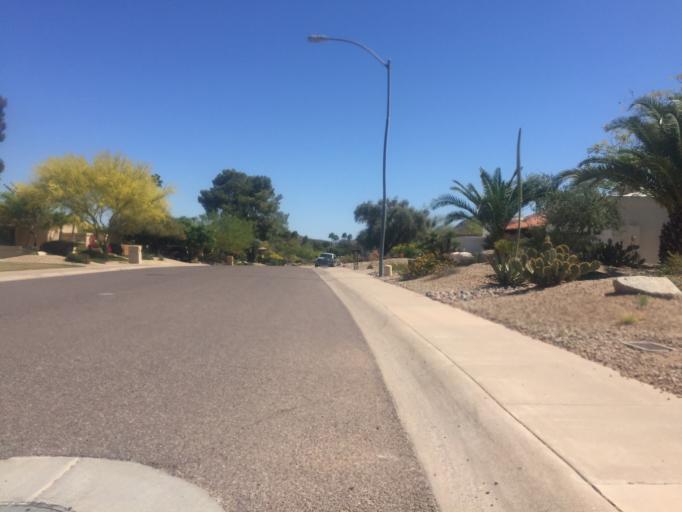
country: US
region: Arizona
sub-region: Maricopa County
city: Paradise Valley
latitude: 33.5674
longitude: -112.0143
